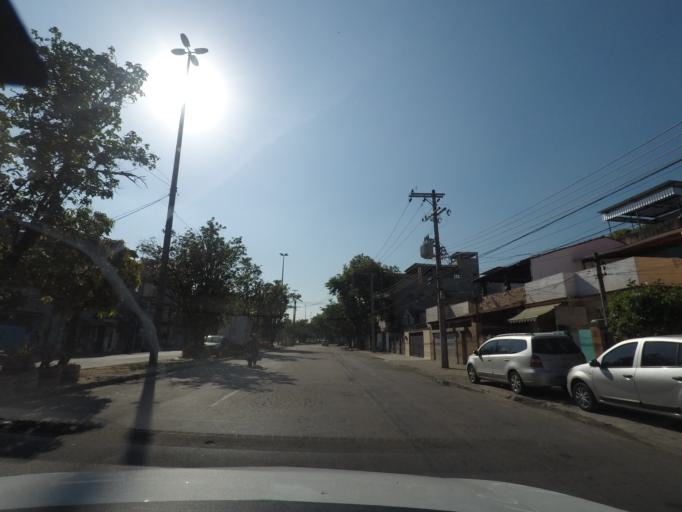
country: BR
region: Rio de Janeiro
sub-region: Rio De Janeiro
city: Rio de Janeiro
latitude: -22.8888
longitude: -43.2450
